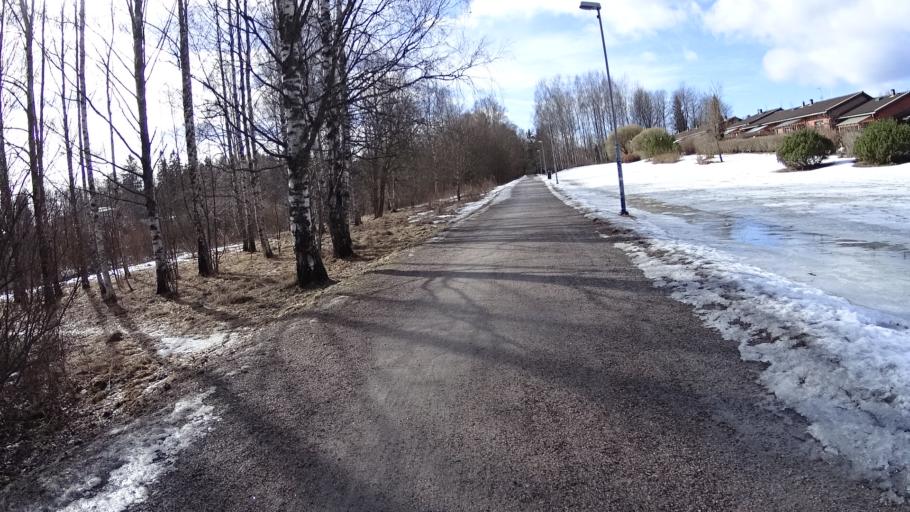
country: FI
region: Uusimaa
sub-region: Helsinki
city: Kauniainen
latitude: 60.2390
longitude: 24.7165
